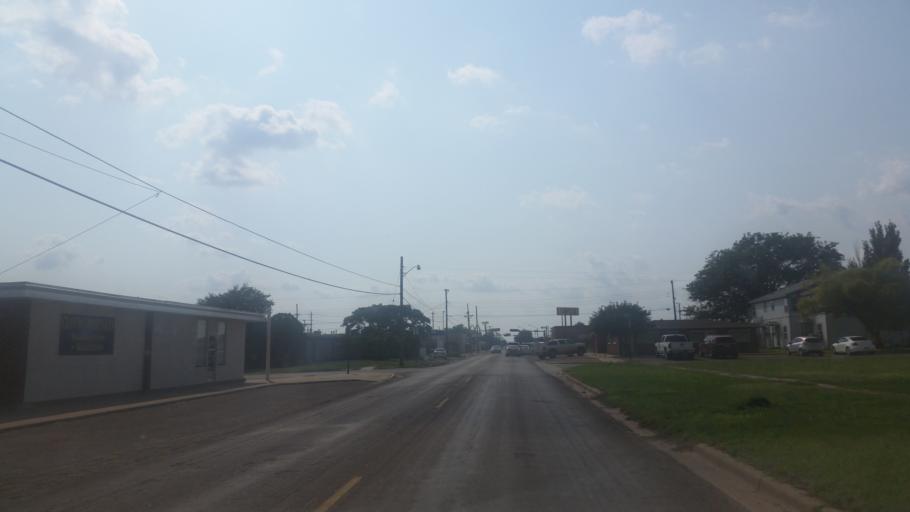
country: US
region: New Mexico
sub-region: Curry County
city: Clovis
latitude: 34.4120
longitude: -103.2035
